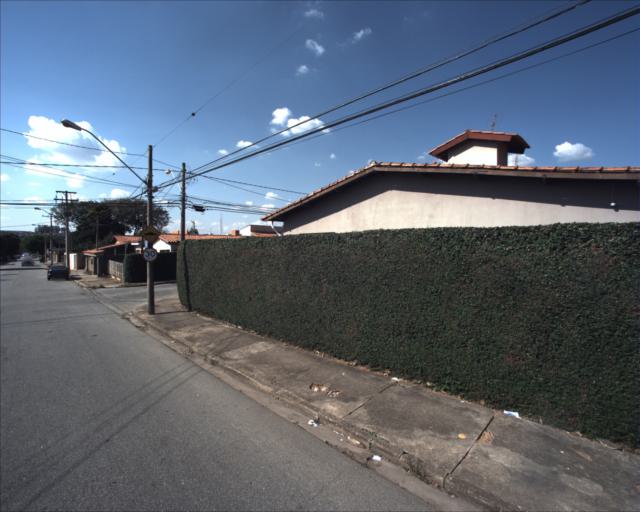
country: BR
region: Sao Paulo
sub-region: Sorocaba
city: Sorocaba
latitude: -23.4747
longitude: -47.4476
